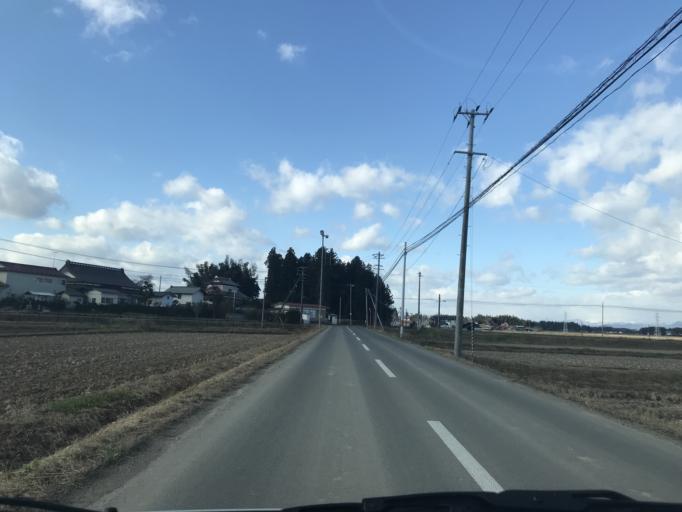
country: JP
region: Miyagi
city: Kogota
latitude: 38.7381
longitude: 141.0620
